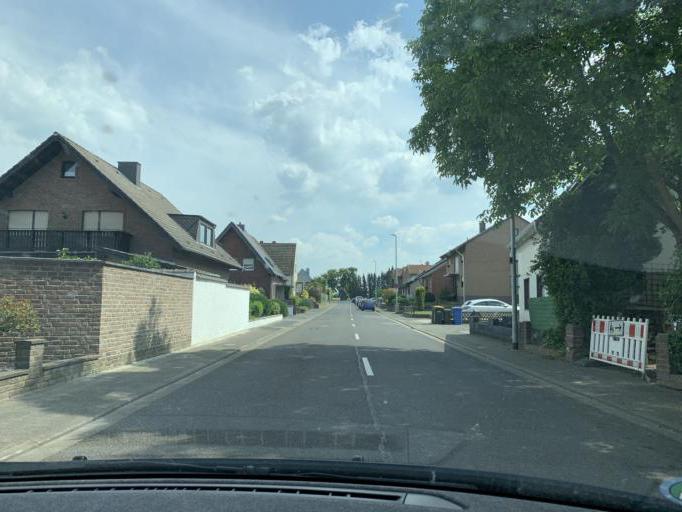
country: DE
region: North Rhine-Westphalia
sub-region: Regierungsbezirk Koln
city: Elsdorf
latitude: 50.9199
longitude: 6.5889
